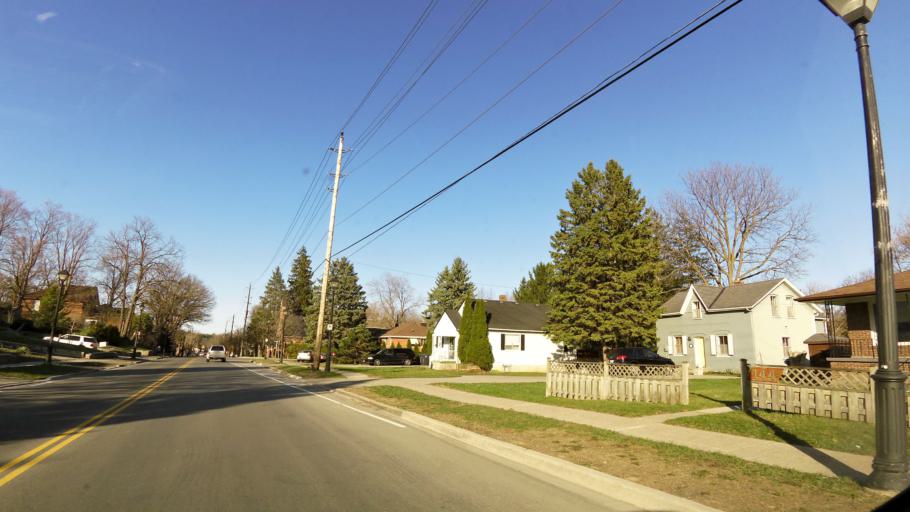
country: CA
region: Ontario
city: Brampton
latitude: 43.8763
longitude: -79.7419
